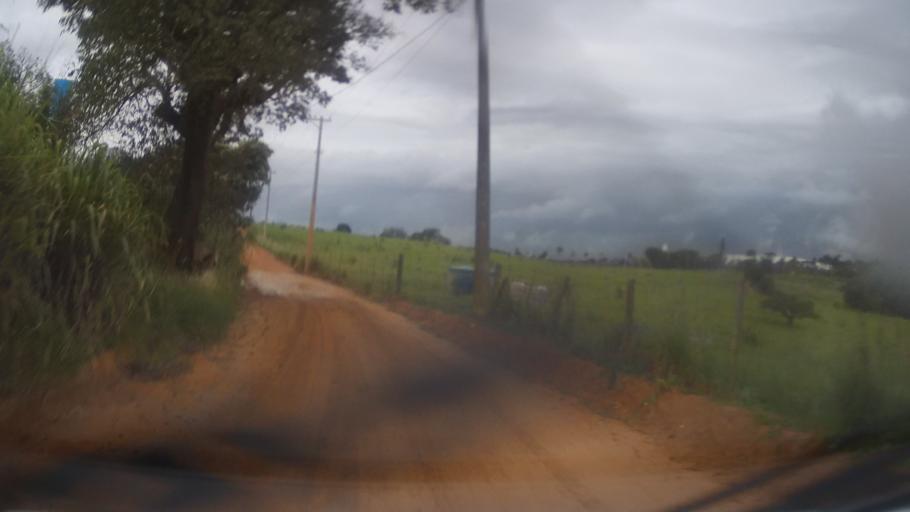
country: BR
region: Sao Paulo
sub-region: Itupeva
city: Itupeva
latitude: -23.1797
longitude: -47.0339
